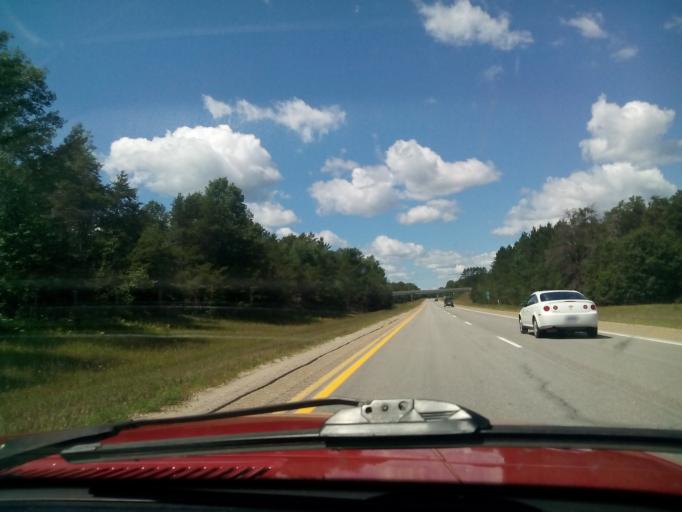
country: US
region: Michigan
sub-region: Roscommon County
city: Roscommon
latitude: 44.4552
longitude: -84.6014
